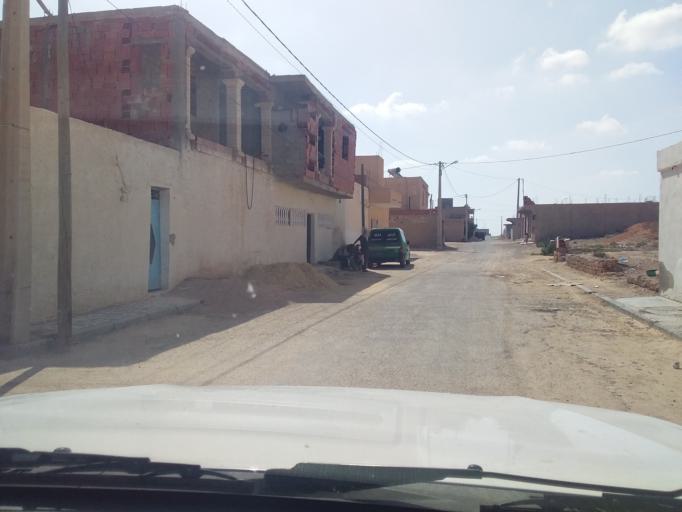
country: TN
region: Madanin
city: Medenine
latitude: 33.5818
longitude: 10.3243
